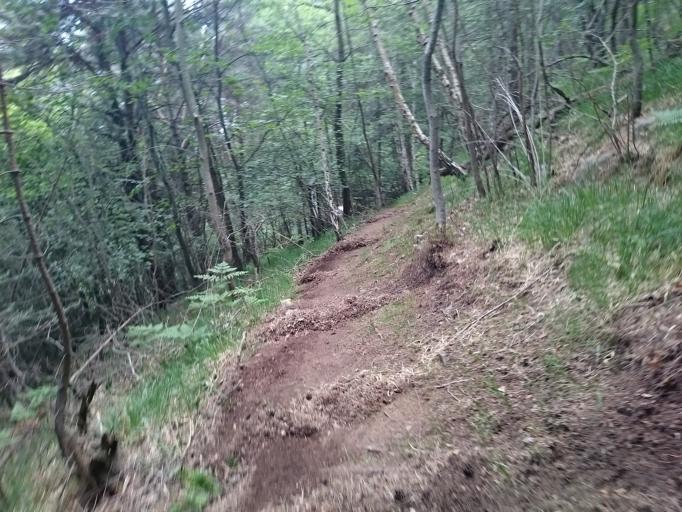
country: IT
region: Lombardy
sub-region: Provincia di Brescia
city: Paspardo
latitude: 46.0385
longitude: 10.3708
